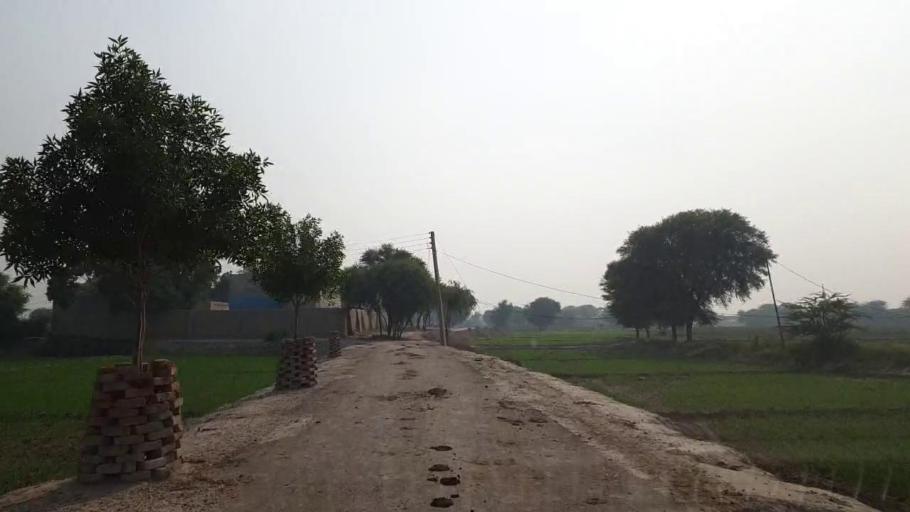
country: PK
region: Sindh
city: Bhan
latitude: 26.5415
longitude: 67.7123
